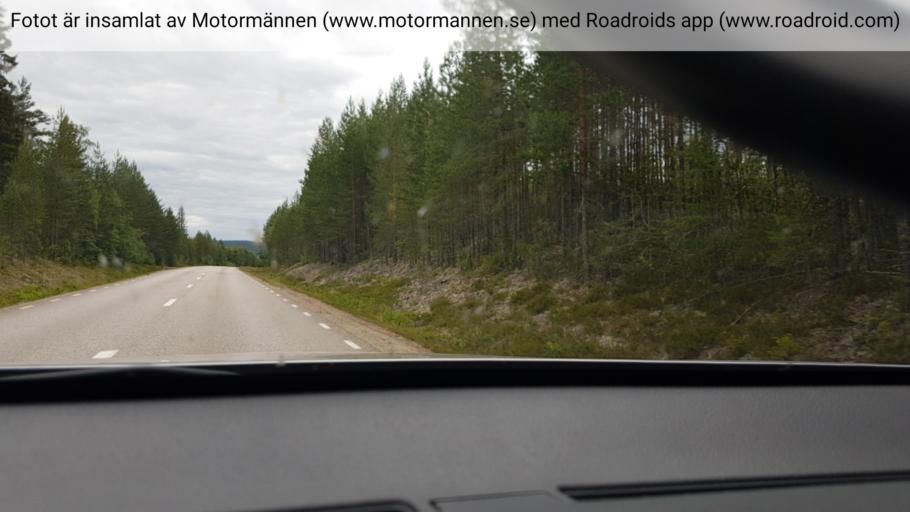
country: NO
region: Hedmark
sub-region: Trysil
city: Innbygda
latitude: 60.9315
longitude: 12.4960
